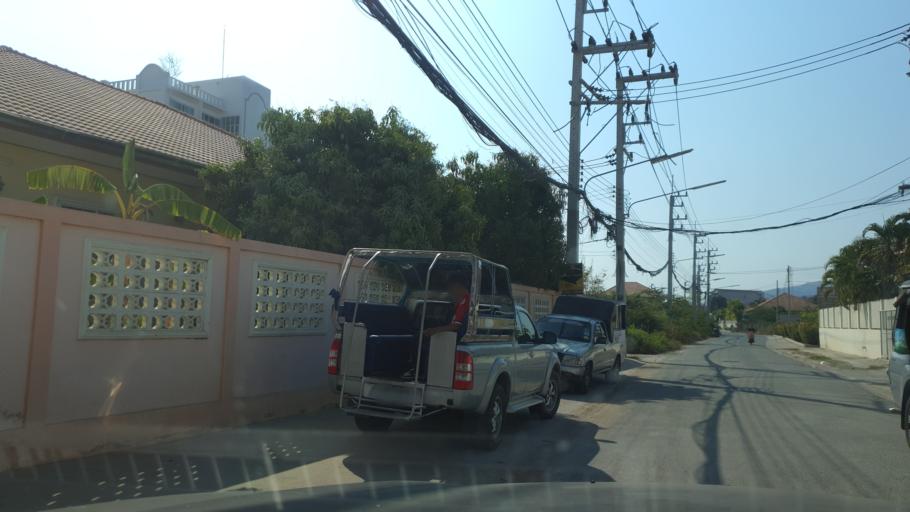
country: TH
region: Prachuap Khiri Khan
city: Hua Hin
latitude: 12.5534
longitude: 99.9540
